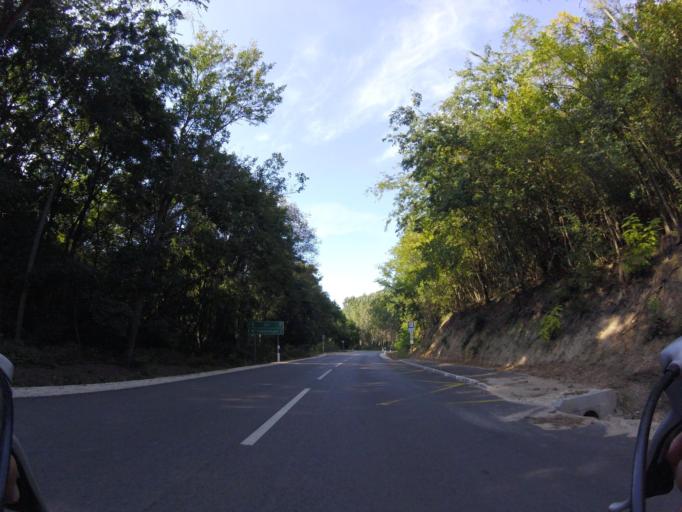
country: HU
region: Pest
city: Gomba
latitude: 47.3883
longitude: 19.5004
